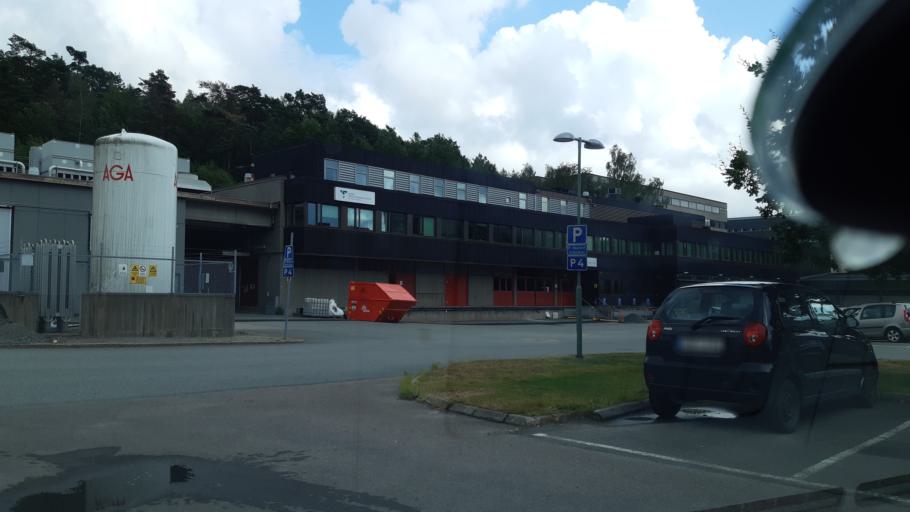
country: SE
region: Vaestra Goetaland
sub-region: Goteborg
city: Eriksbo
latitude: 57.7232
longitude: 12.0525
